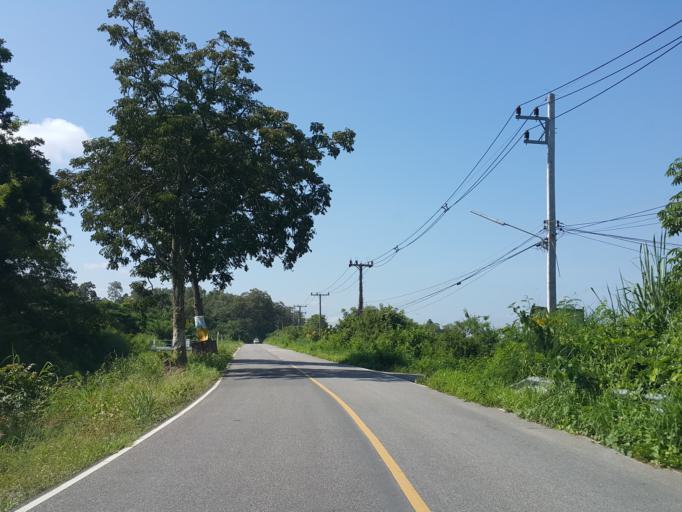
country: TH
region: Chiang Mai
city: San Kamphaeng
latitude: 18.7747
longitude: 99.1745
